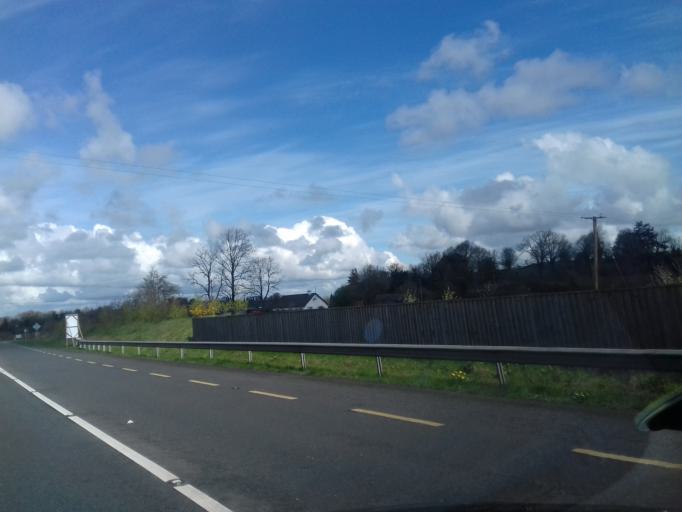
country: IE
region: Ulster
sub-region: An Cabhan
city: Belturbet
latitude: 54.0684
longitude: -7.4053
